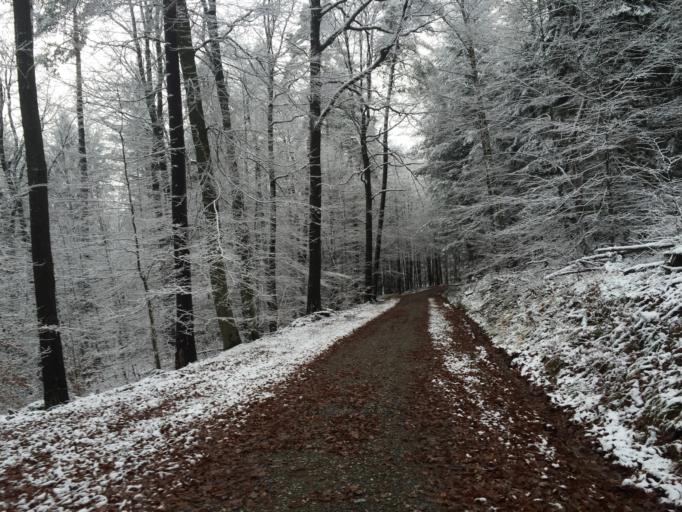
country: DE
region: Hesse
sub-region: Regierungsbezirk Darmstadt
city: Wald-Michelbach
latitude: 49.5707
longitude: 8.8739
